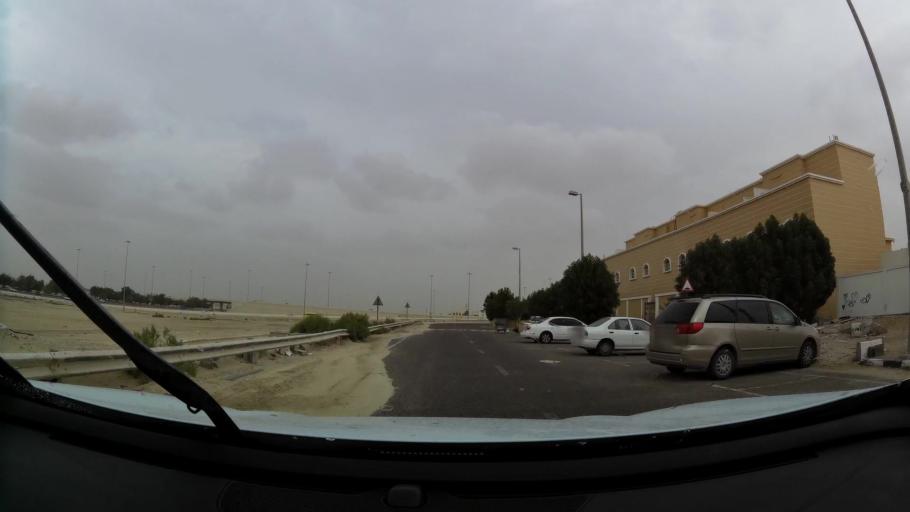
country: AE
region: Abu Dhabi
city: Abu Dhabi
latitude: 24.3650
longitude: 54.6550
